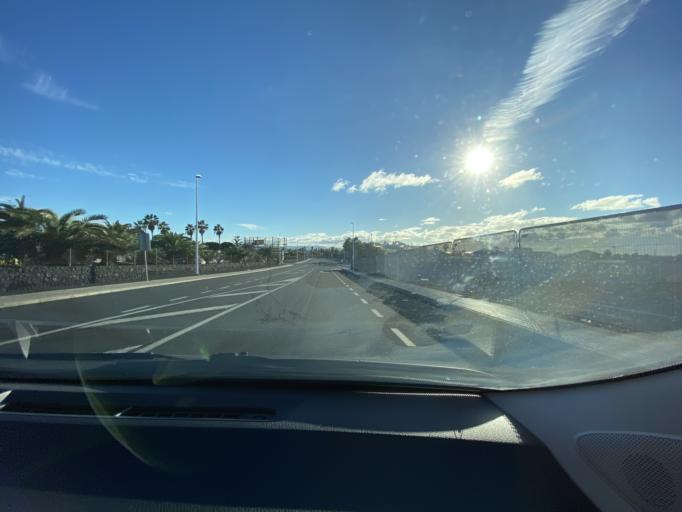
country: ES
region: Canary Islands
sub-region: Provincia de Las Palmas
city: Playa Blanca
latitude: 28.8639
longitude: -13.8417
